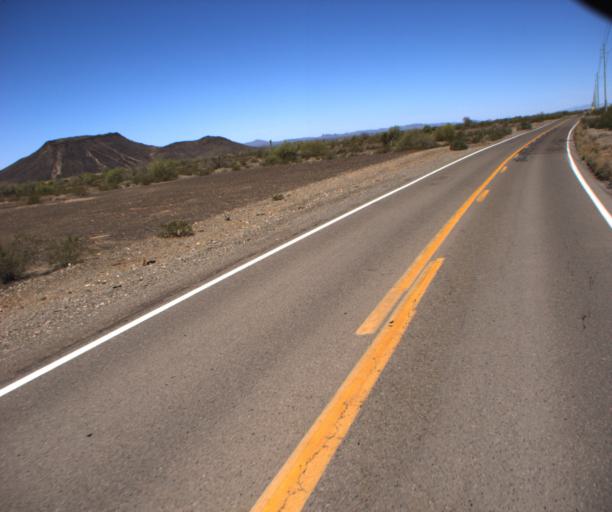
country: US
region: Arizona
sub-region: La Paz County
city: Salome
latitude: 33.7530
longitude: -113.7730
